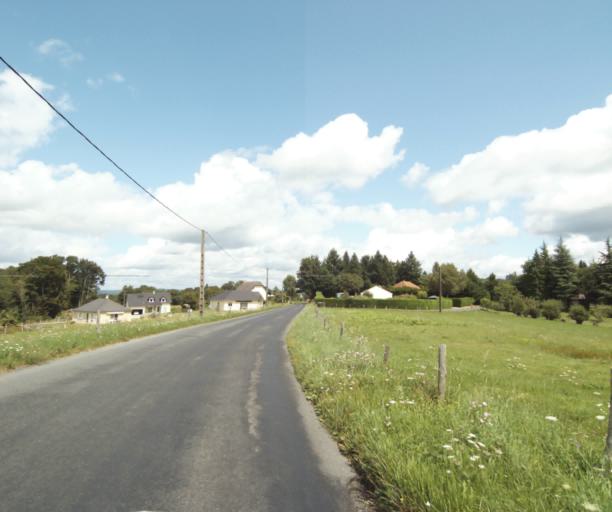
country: FR
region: Limousin
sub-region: Departement de la Correze
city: Sainte-Fortunade
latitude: 45.1998
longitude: 1.8249
